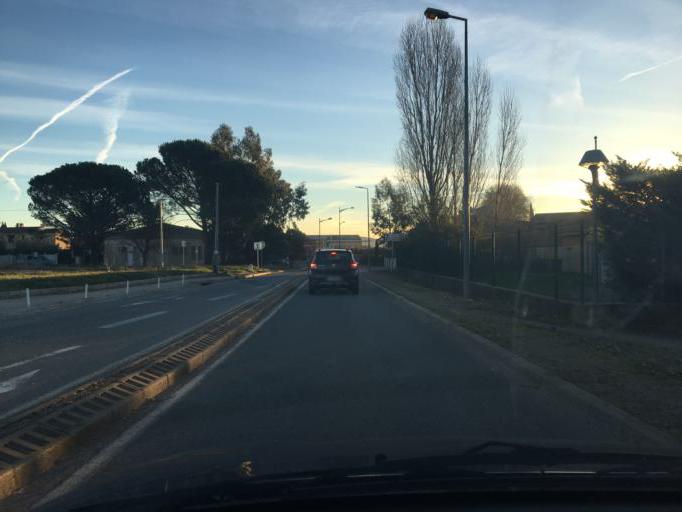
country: FR
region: Provence-Alpes-Cote d'Azur
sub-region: Departement du Var
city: Les Arcs
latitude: 43.4489
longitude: 6.4739
